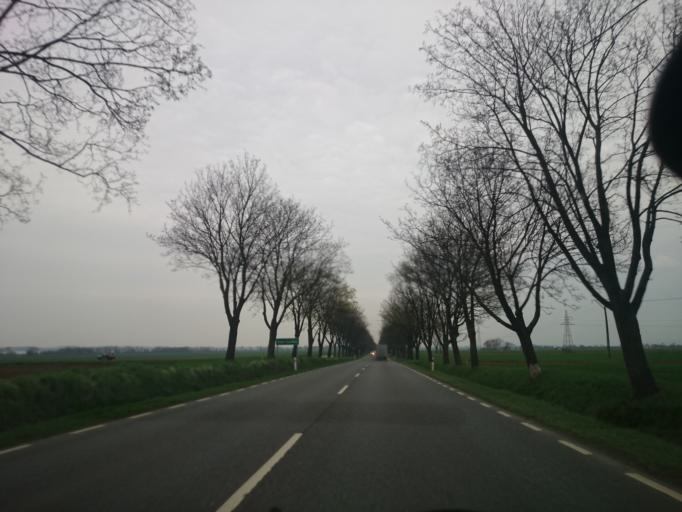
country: PL
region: Opole Voivodeship
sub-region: Powiat nyski
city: Paczkow
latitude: 50.4527
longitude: 17.0529
